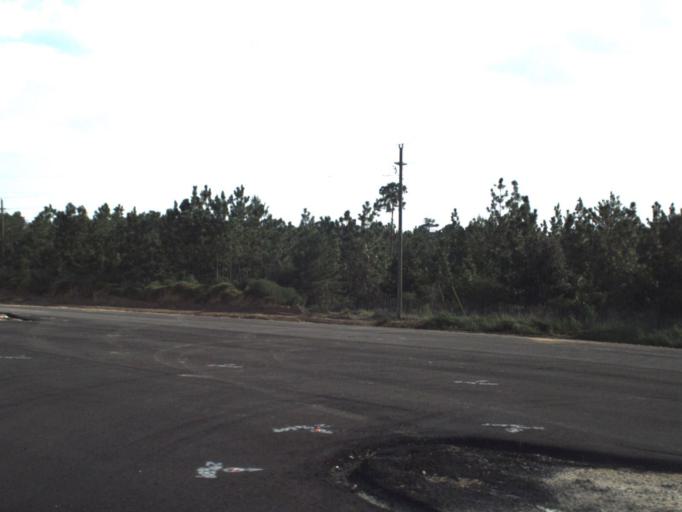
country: US
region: Florida
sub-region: Walton County
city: DeFuniak Springs
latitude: 30.6122
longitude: -86.1149
